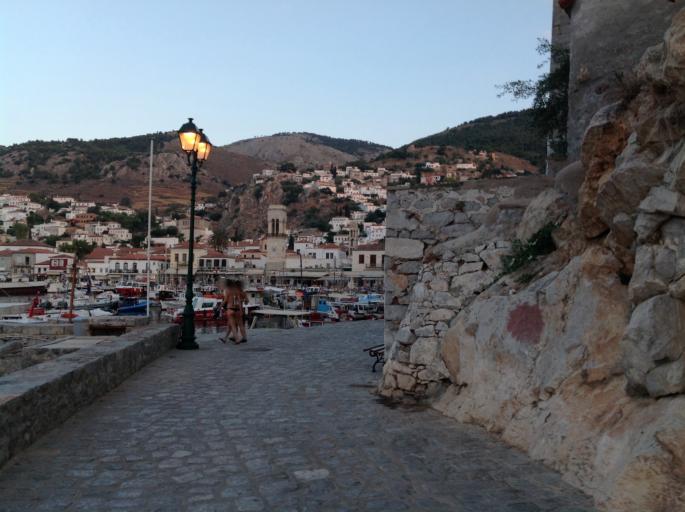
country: GR
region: Attica
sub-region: Nomos Piraios
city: Ydra
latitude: 37.3511
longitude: 23.4647
